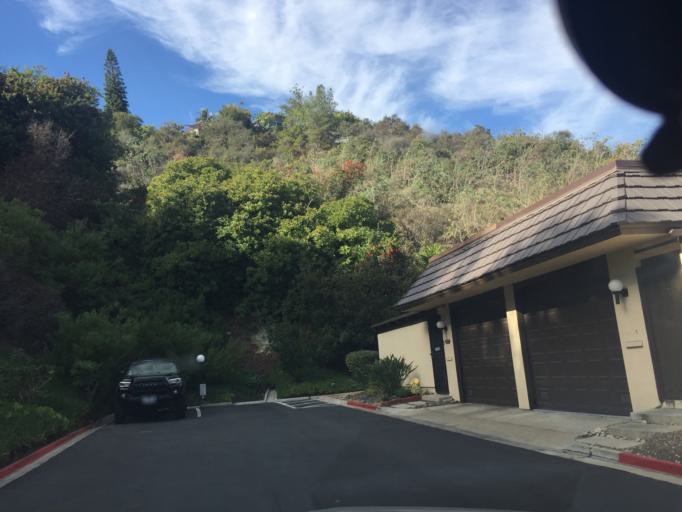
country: US
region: California
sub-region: San Diego County
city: Lemon Grove
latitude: 32.7675
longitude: -117.0860
